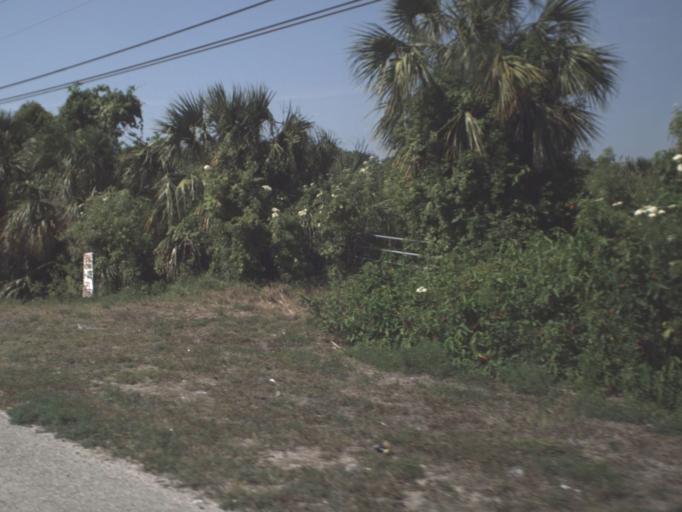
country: US
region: Florida
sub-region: Brevard County
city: Rockledge
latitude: 28.3089
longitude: -80.7074
